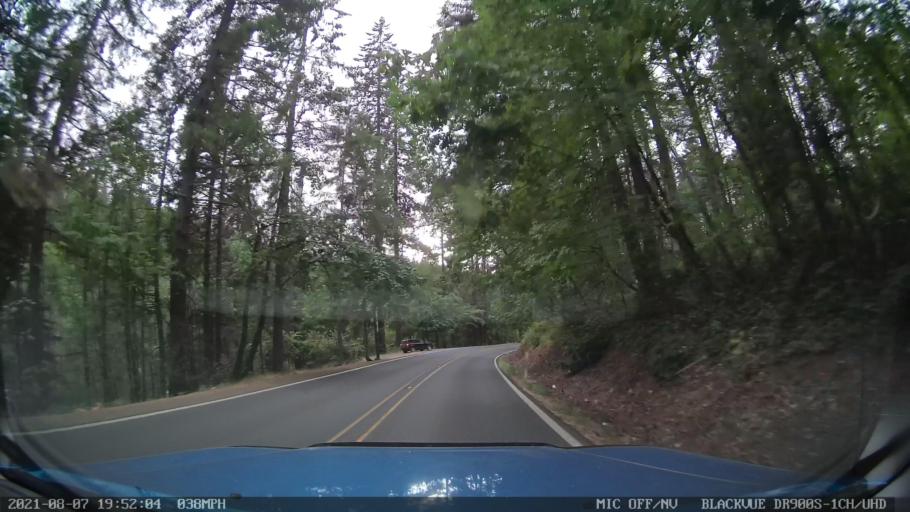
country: US
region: Oregon
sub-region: Marion County
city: Silverton
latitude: 44.9835
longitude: -122.7531
